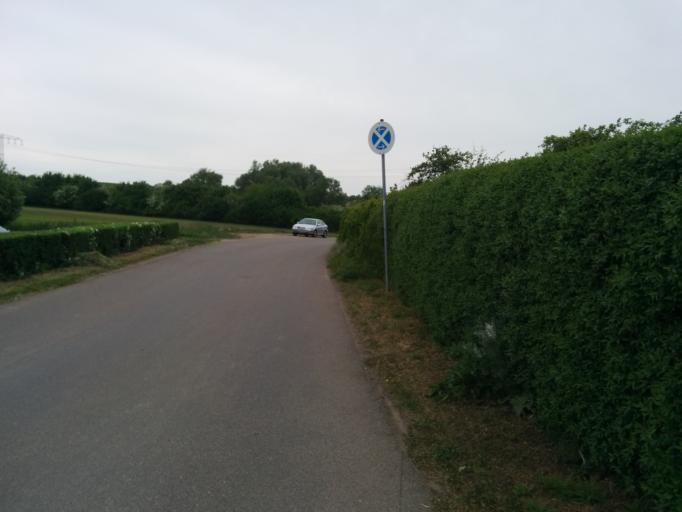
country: DE
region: Saxony-Anhalt
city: Zscherben
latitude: 51.4609
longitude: 11.8719
